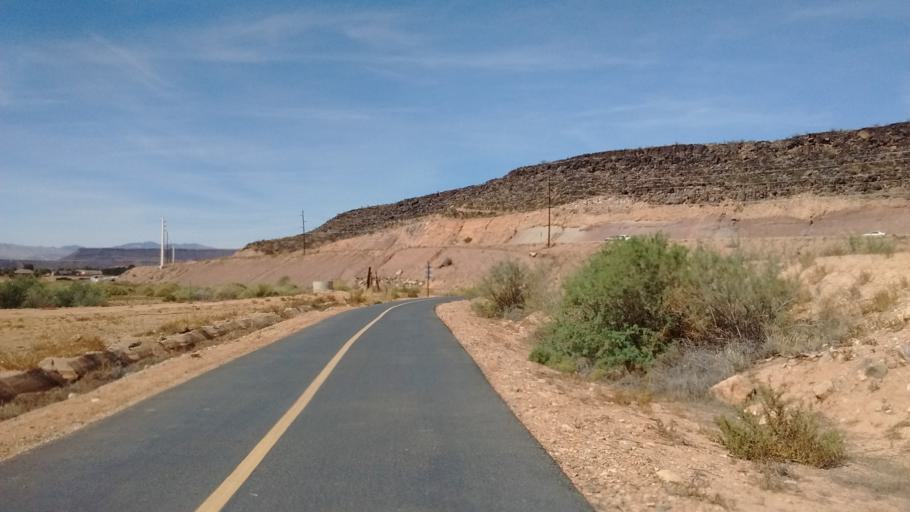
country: US
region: Utah
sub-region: Washington County
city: Saint George
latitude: 37.0871
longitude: -113.5452
